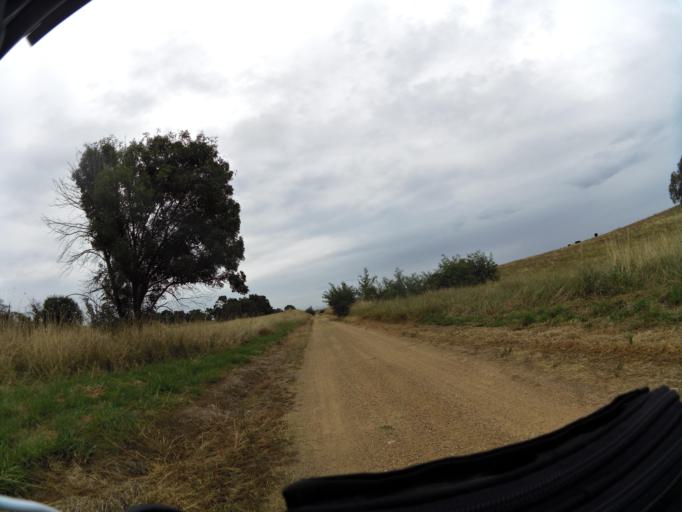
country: AU
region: New South Wales
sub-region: Albury Municipality
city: East Albury
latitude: -36.2069
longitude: 147.0523
